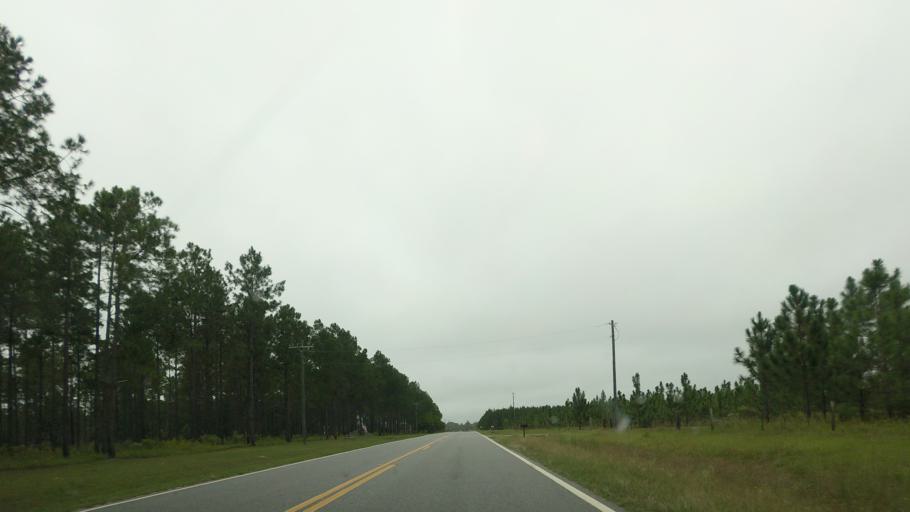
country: US
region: Georgia
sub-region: Berrien County
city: Enigma
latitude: 31.4439
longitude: -83.2400
